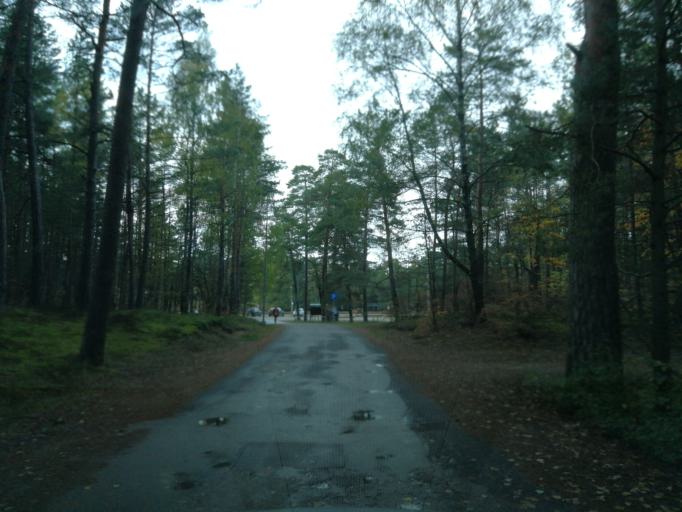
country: LV
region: Riga
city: Jaunciems
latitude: 57.0851
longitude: 24.1542
